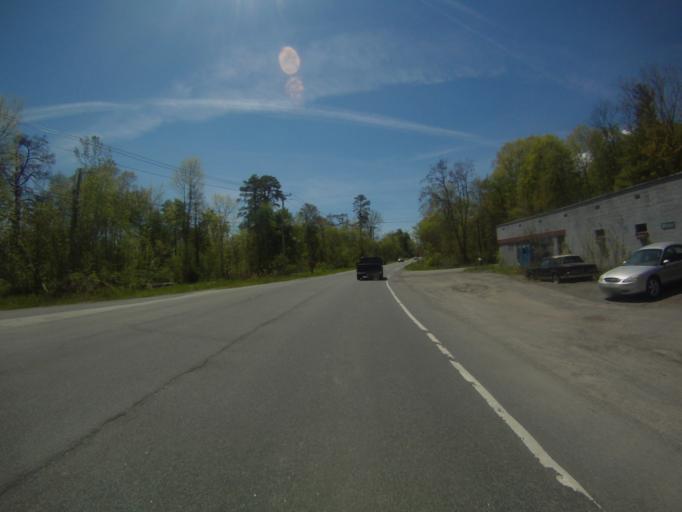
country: US
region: New York
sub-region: Essex County
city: Ticonderoga
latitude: 43.9480
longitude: -73.4178
